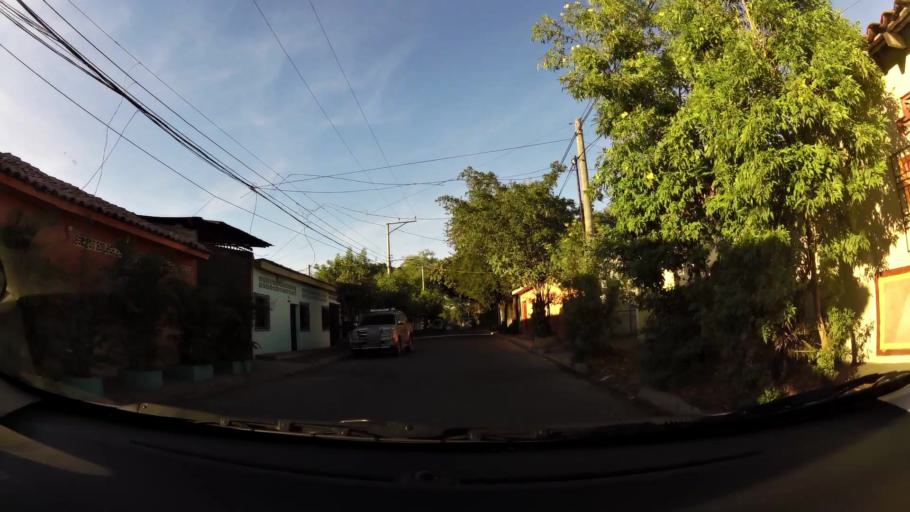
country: SV
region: San Miguel
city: San Miguel
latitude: 13.4658
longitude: -88.1689
